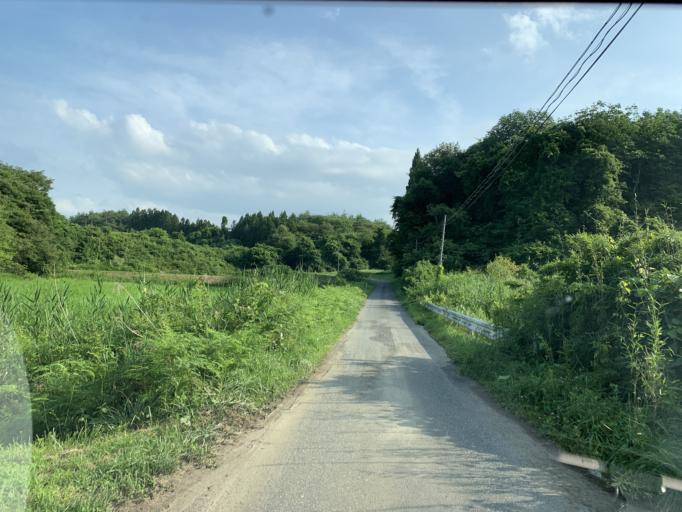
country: JP
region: Iwate
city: Ichinoseki
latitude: 38.8540
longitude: 141.1152
